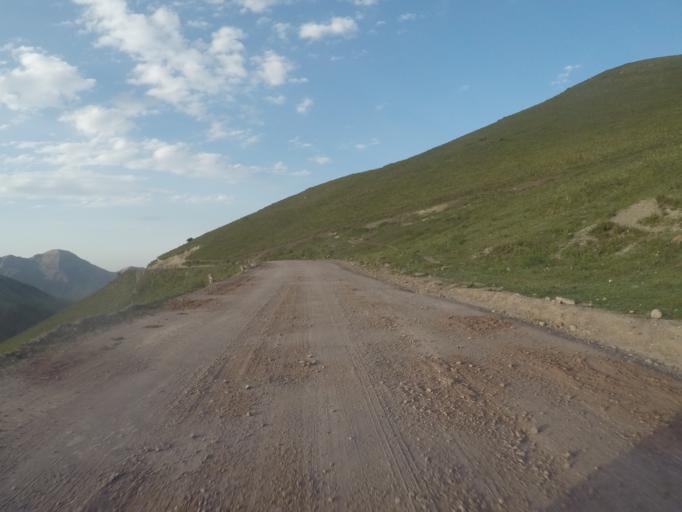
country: KG
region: Chuy
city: Bishkek
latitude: 42.6417
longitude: 74.6427
